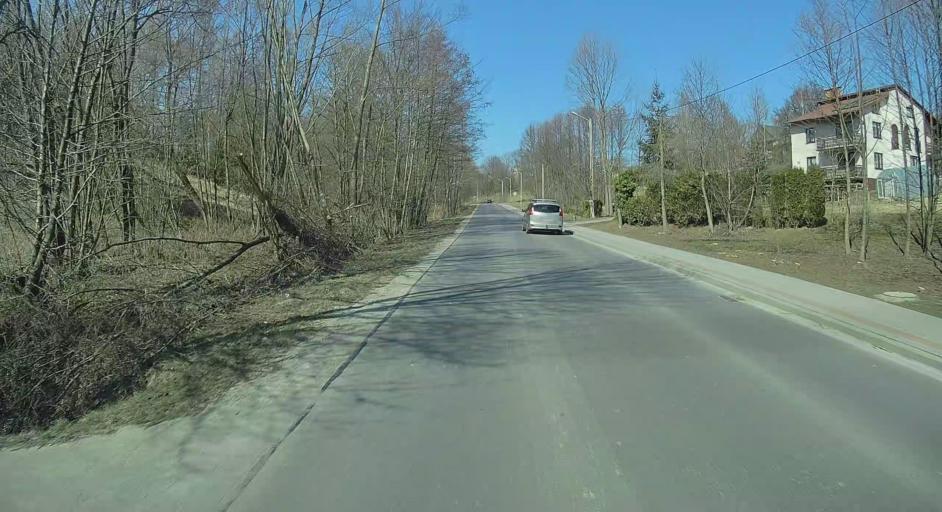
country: PL
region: Subcarpathian Voivodeship
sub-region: Powiat rzeszowski
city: Hyzne
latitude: 49.8890
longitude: 22.2276
